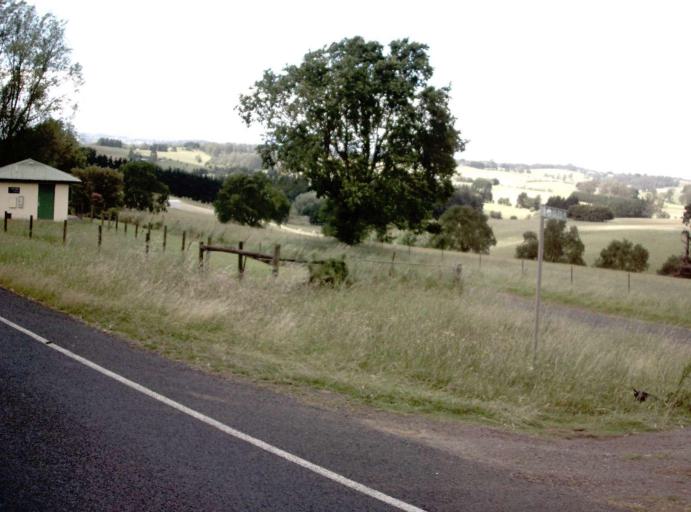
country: AU
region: Victoria
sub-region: Baw Baw
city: Warragul
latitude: -38.0986
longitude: 145.9219
